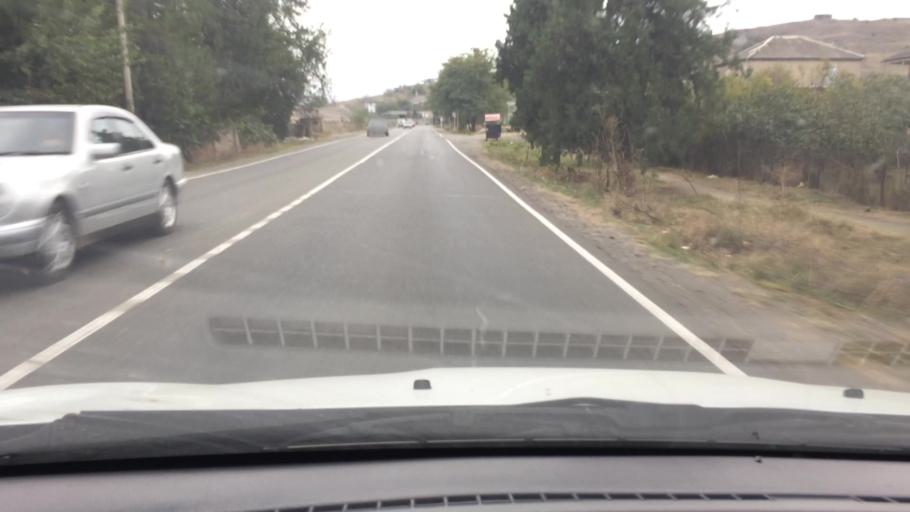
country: GE
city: Naghvarevi
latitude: 41.3704
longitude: 44.8368
